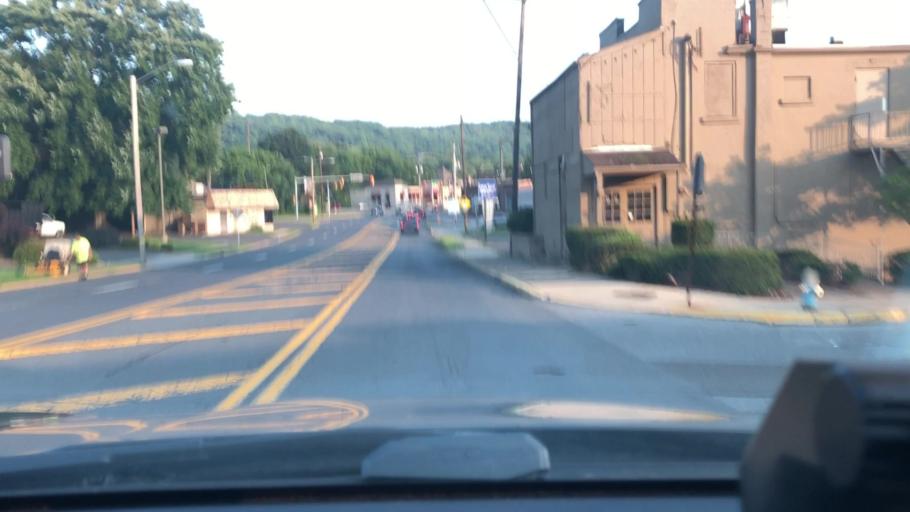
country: US
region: Pennsylvania
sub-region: Lehigh County
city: Emmaus
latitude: 40.5441
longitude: -75.4871
